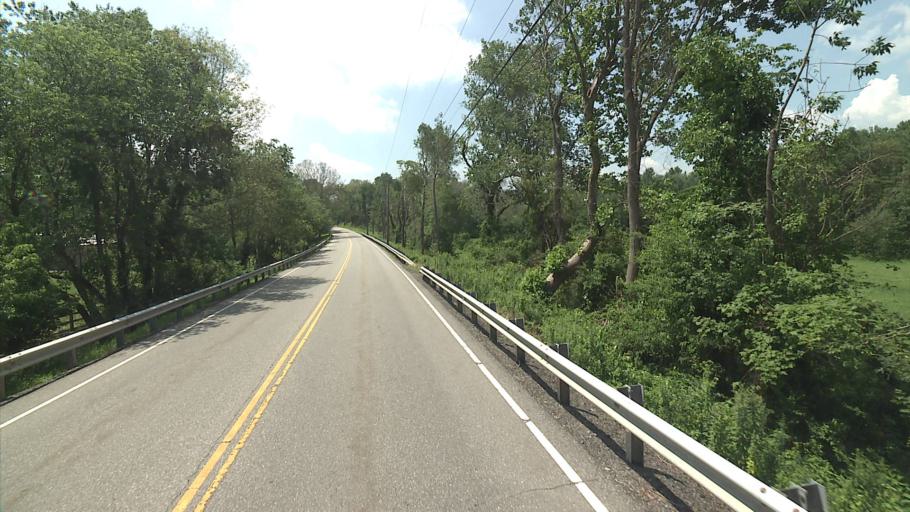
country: US
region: Connecticut
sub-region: New London County
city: Preston City
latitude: 41.5464
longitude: -71.9124
